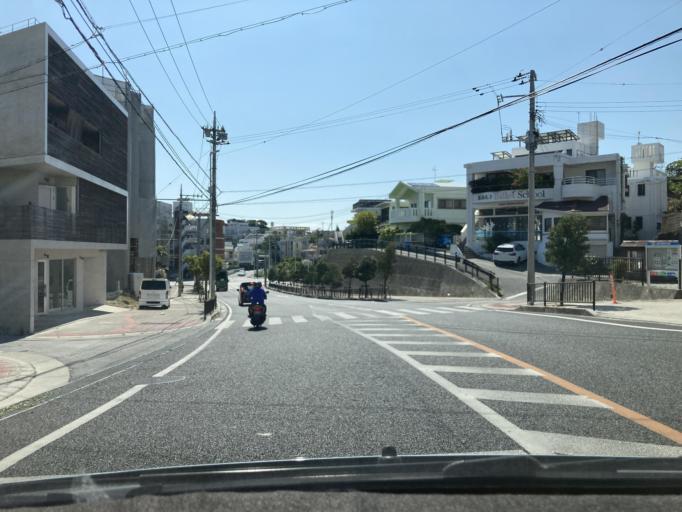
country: JP
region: Okinawa
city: Naha-shi
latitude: 26.2288
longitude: 127.7189
